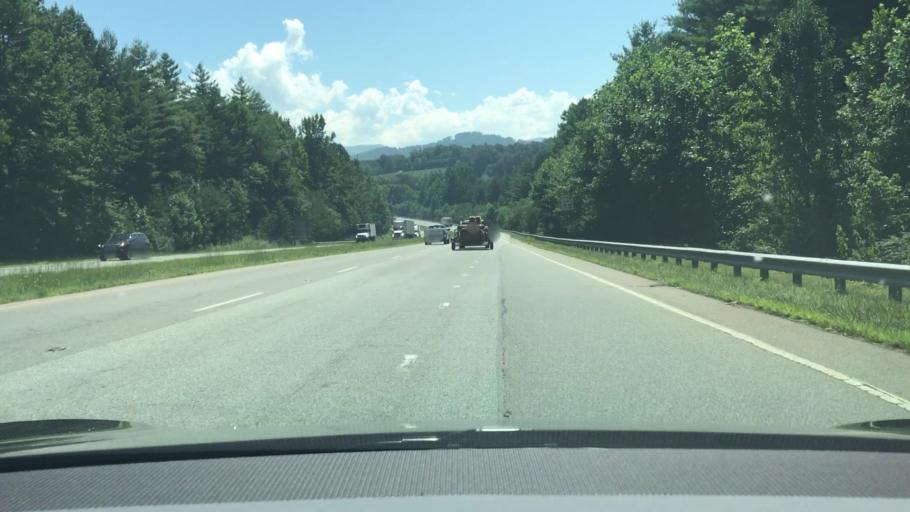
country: US
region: North Carolina
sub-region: Macon County
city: Franklin
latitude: 35.1648
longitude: -83.3824
